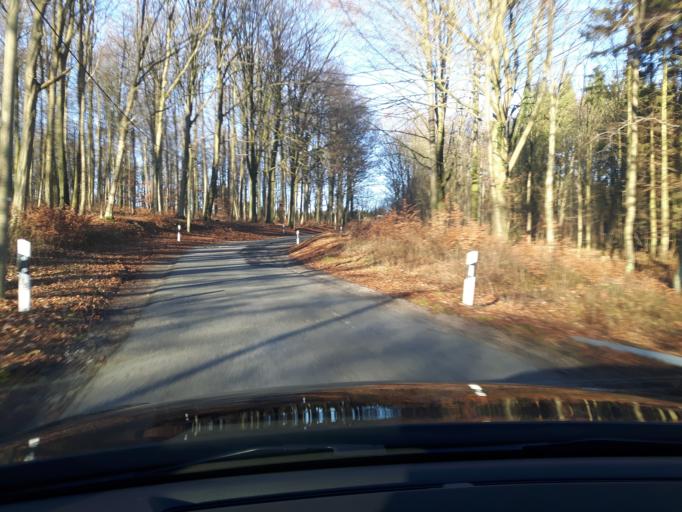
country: DE
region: Mecklenburg-Vorpommern
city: Putbus
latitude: 54.3617
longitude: 13.4393
